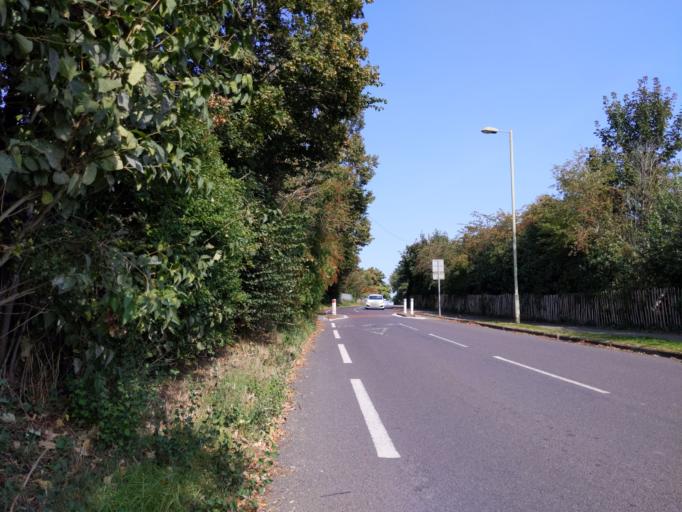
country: GB
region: England
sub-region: Oxfordshire
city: Cowley
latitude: 51.7187
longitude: -1.2274
